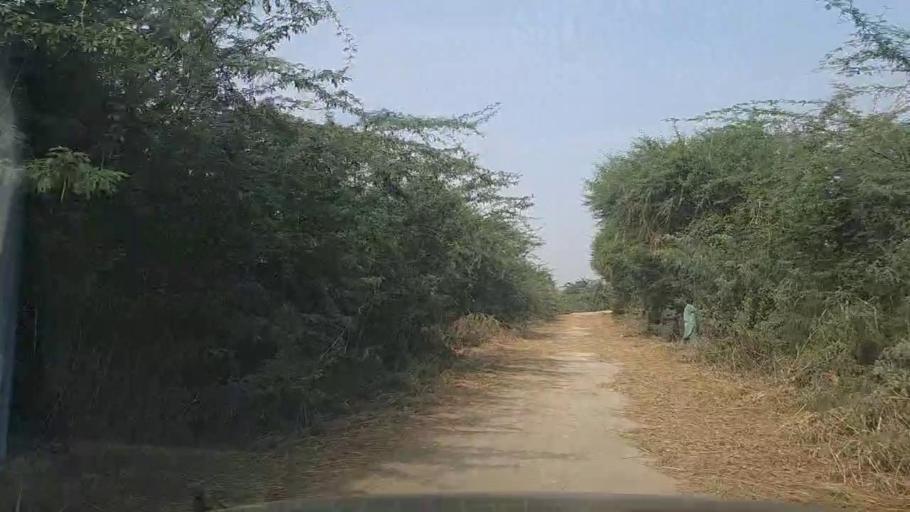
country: PK
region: Sindh
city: Bulri
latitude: 24.9800
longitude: 68.2934
